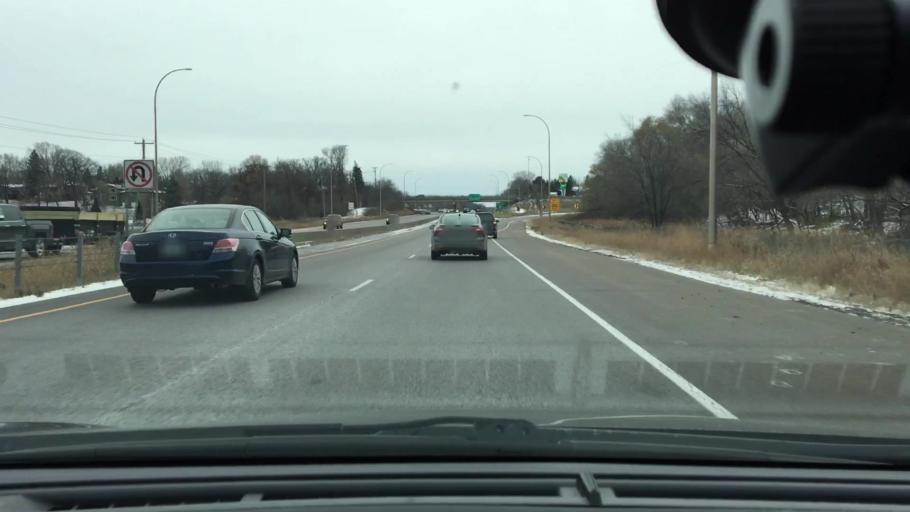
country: US
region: Minnesota
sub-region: Hennepin County
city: New Hope
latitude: 45.0725
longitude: -93.4015
